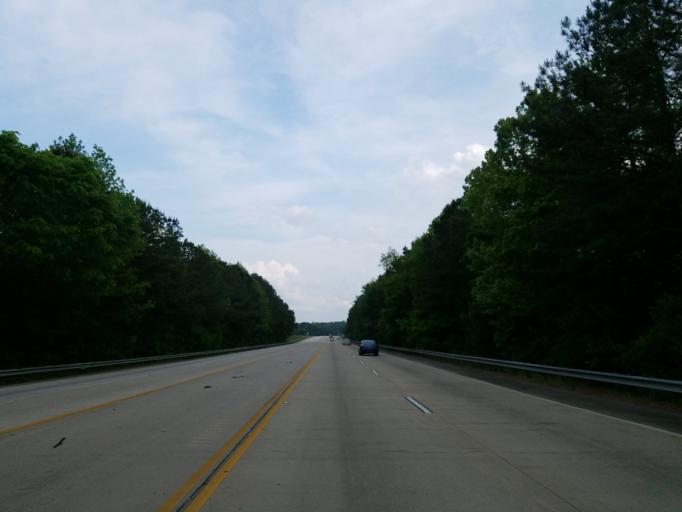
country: US
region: Georgia
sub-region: Douglas County
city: Lithia Springs
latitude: 33.8247
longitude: -84.6633
